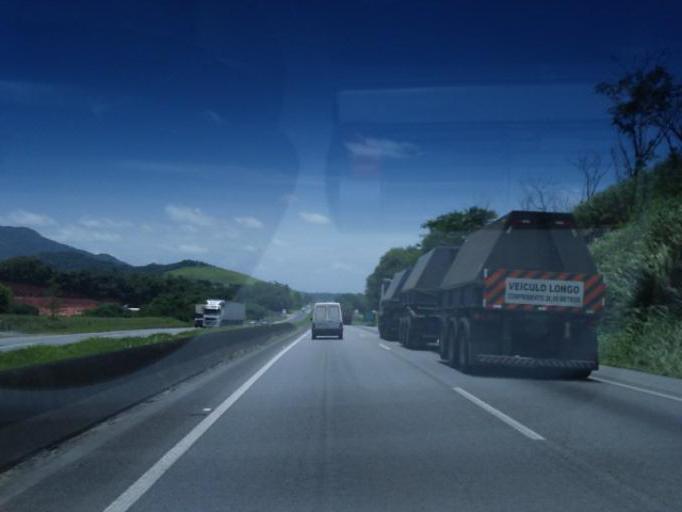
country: BR
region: Sao Paulo
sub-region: Juquia
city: Juquia
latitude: -24.3236
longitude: -47.5497
